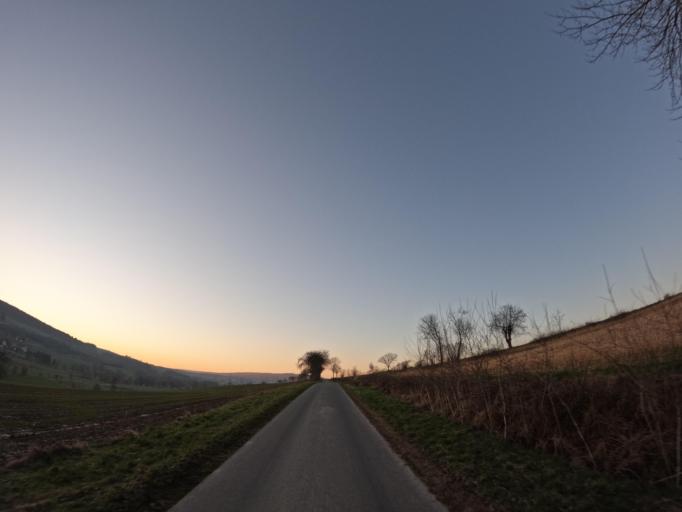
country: DE
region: Lower Saxony
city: Bodenfelde
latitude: 51.6811
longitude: 9.5860
